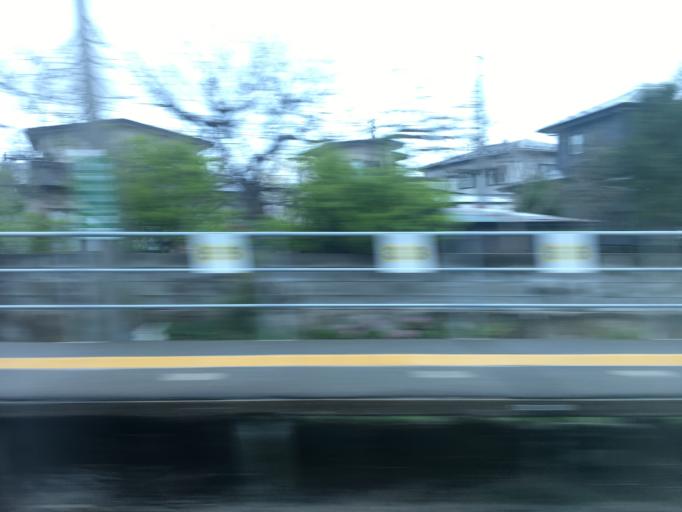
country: JP
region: Akita
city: Akita Shi
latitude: 39.7797
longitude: 140.0684
